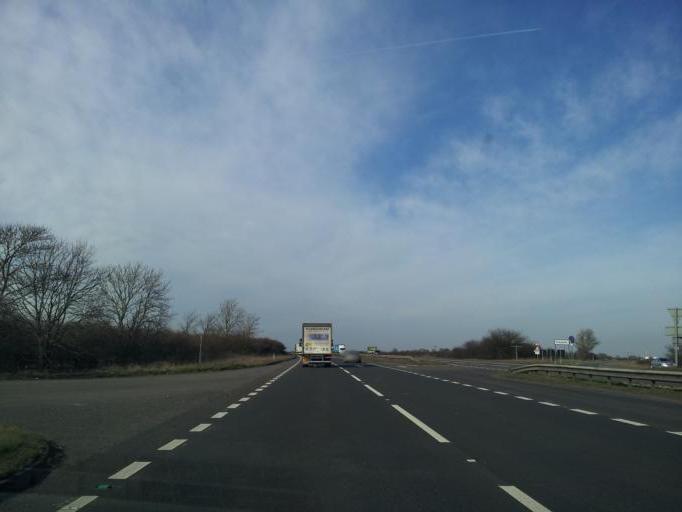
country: GB
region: England
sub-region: Lincolnshire
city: Long Bennington
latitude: 53.0298
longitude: -0.7704
